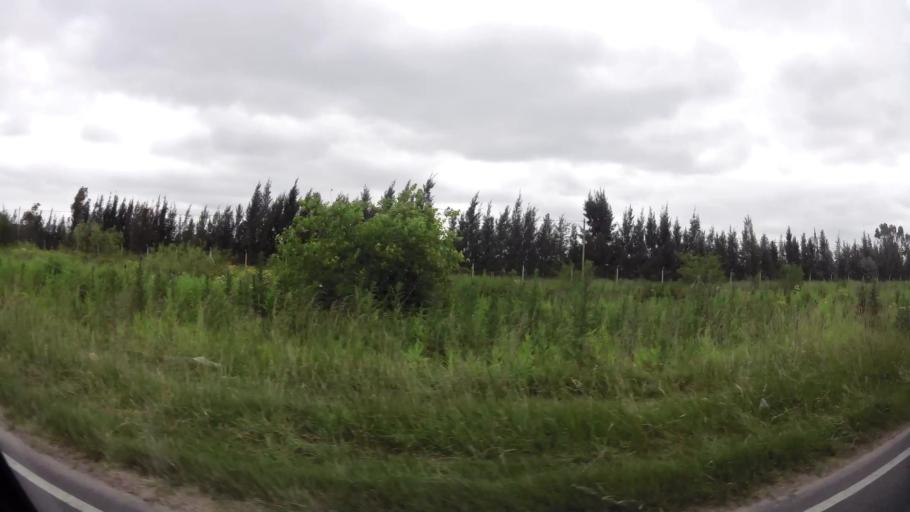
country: AR
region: Buenos Aires
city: Guernica
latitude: -34.9457
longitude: -58.4691
